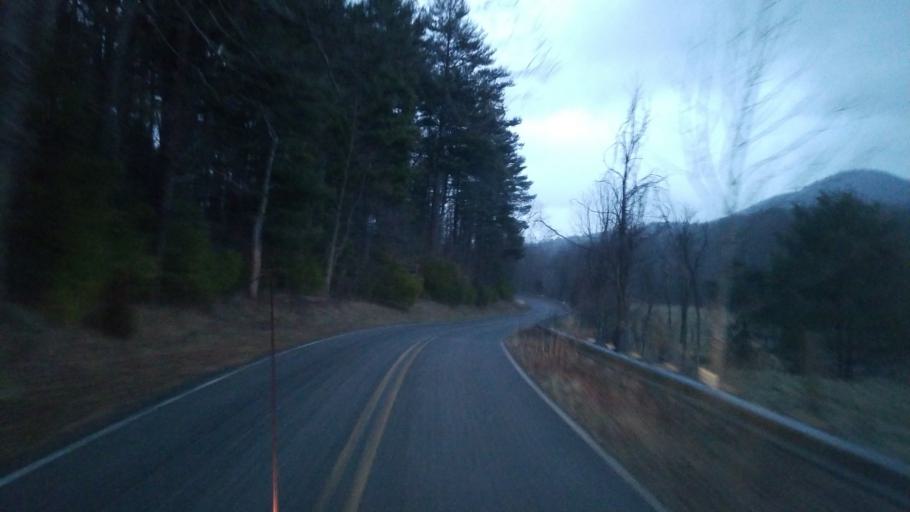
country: US
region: Virginia
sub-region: Pulaski County
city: Pulaski
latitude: 37.1211
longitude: -80.8713
